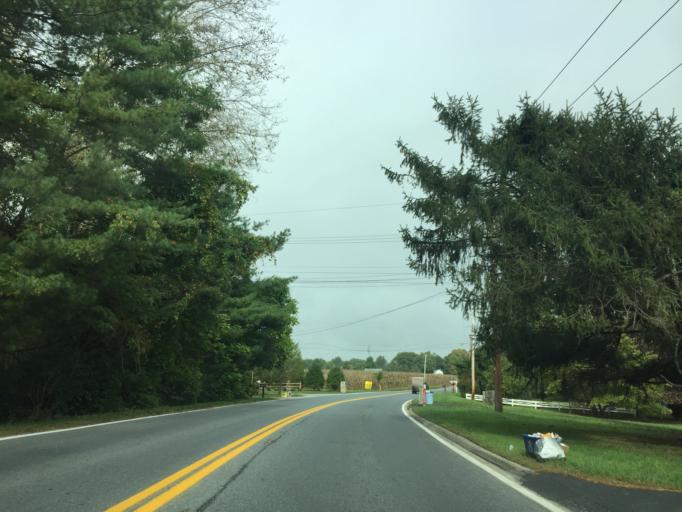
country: US
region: Maryland
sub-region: Baltimore County
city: Garrison
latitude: 39.4489
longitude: -76.7235
